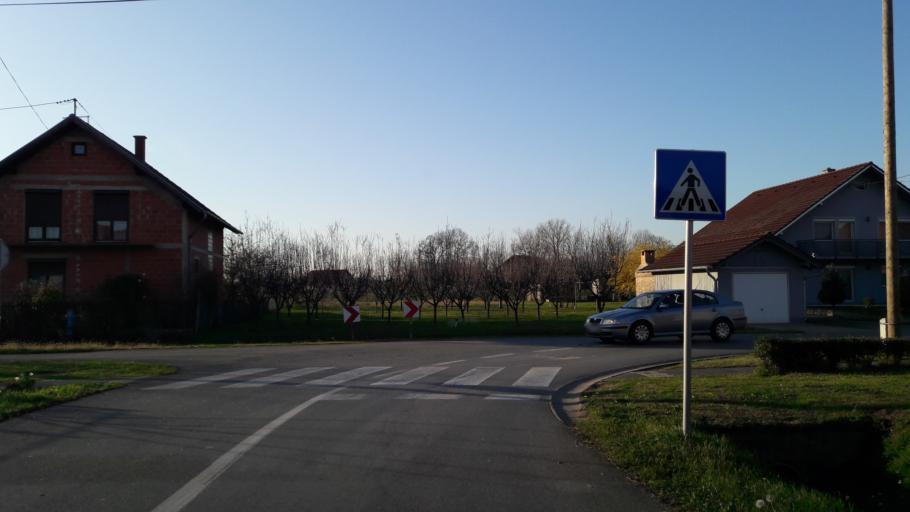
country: HR
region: Osjecko-Baranjska
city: Vuka
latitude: 45.4256
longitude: 18.5009
